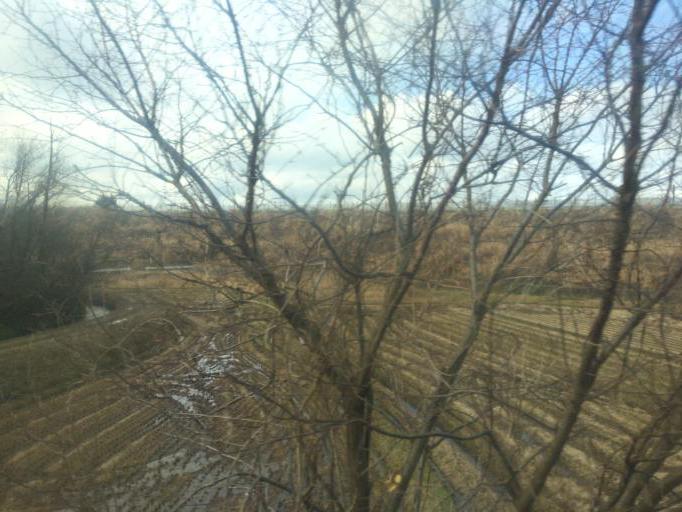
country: JP
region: Akita
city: Noshiromachi
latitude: 40.1758
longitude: 140.0585
